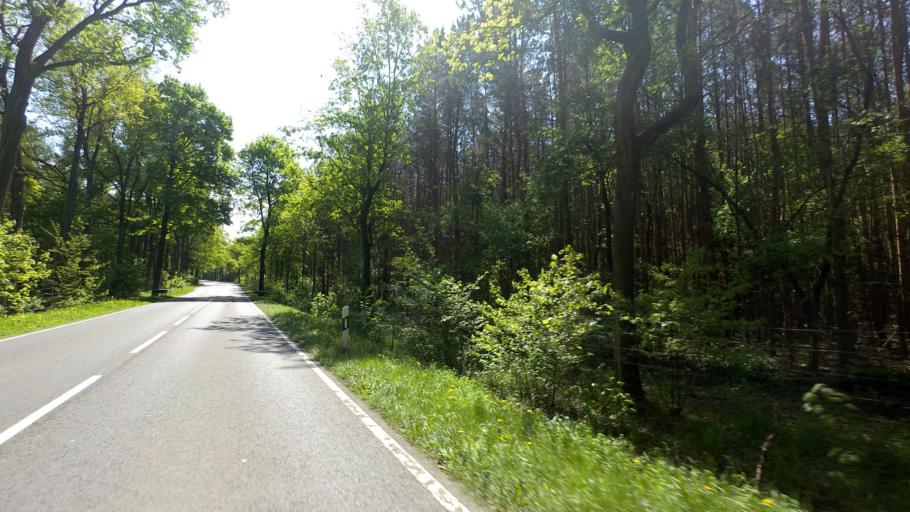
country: DE
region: Brandenburg
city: Schulzendorf
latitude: 52.3218
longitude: 13.5876
